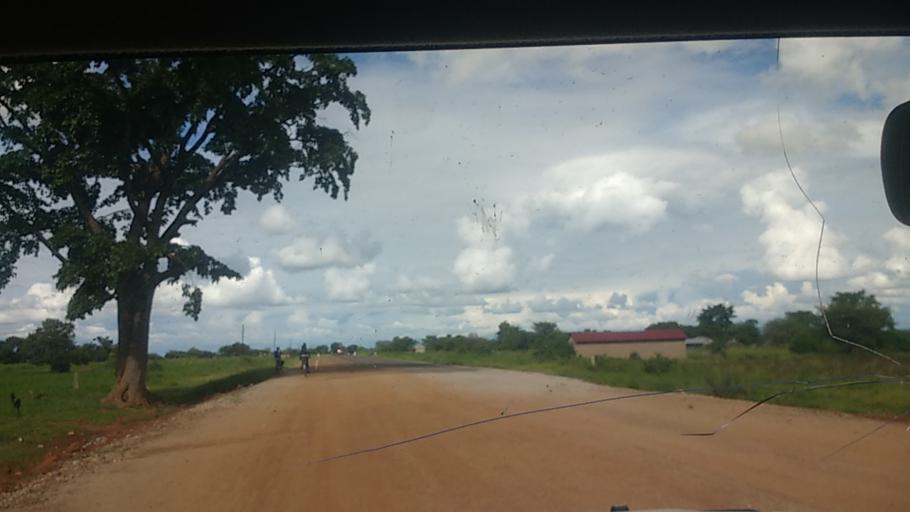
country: UG
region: Eastern Region
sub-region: Katakwi District
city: Katakwi
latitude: 1.9203
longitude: 33.9922
